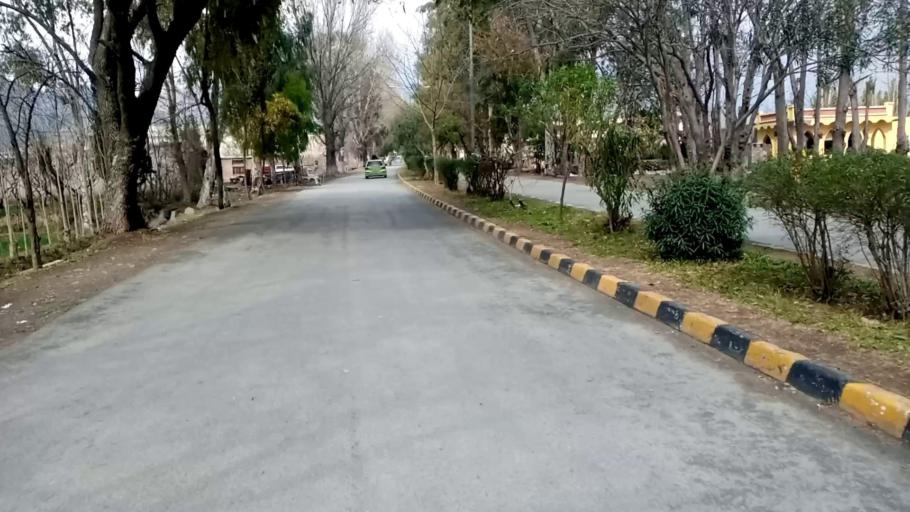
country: PK
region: Khyber Pakhtunkhwa
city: Mingora
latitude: 34.8139
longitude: 72.3415
